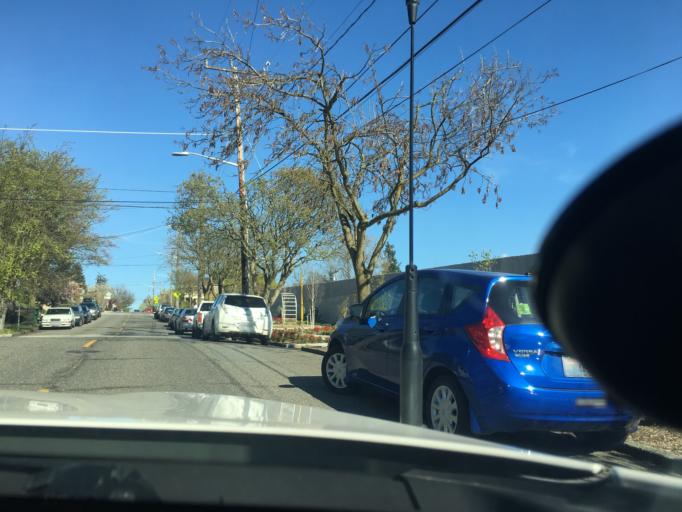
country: US
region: Washington
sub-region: King County
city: Seattle
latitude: 47.6492
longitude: -122.3406
